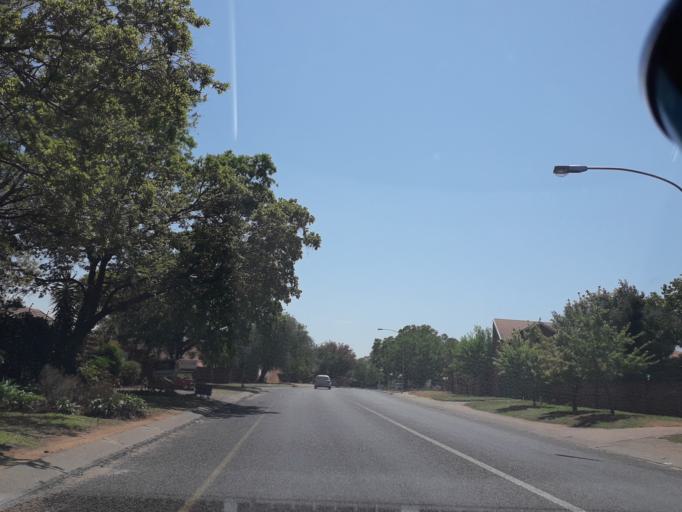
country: ZA
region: Gauteng
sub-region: City of Tshwane Metropolitan Municipality
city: Centurion
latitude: -25.8925
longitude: 28.1469
